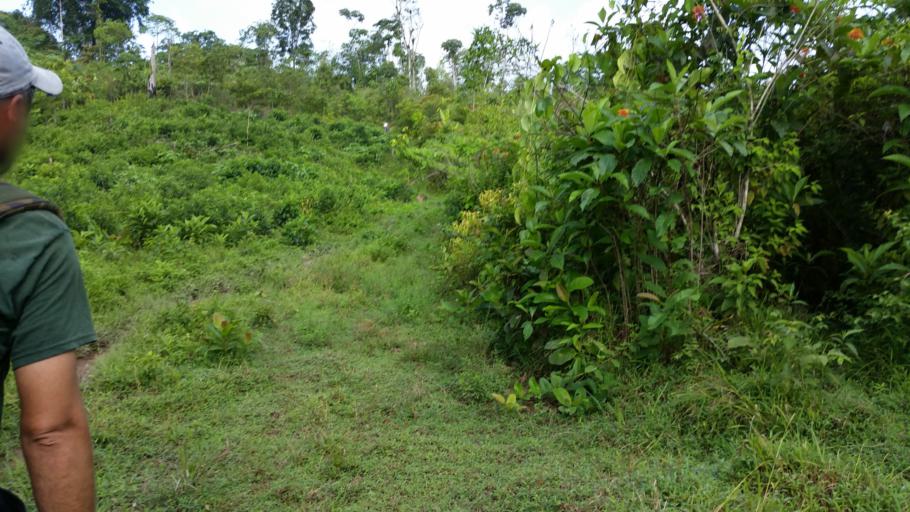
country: NI
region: Atlantico Norte (RAAN)
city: Bonanza
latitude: 14.0914
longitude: -84.6853
